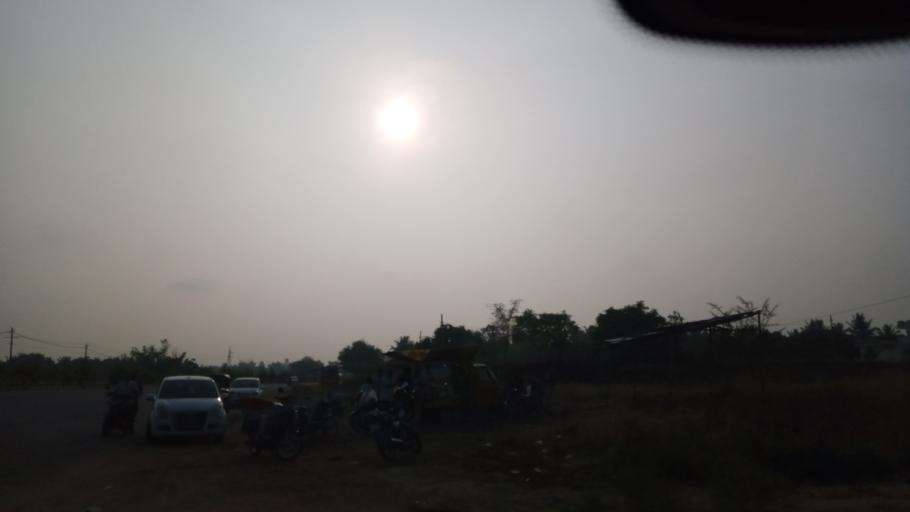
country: IN
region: Karnataka
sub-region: Tumkur
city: Kunigal
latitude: 13.0347
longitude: 77.0871
